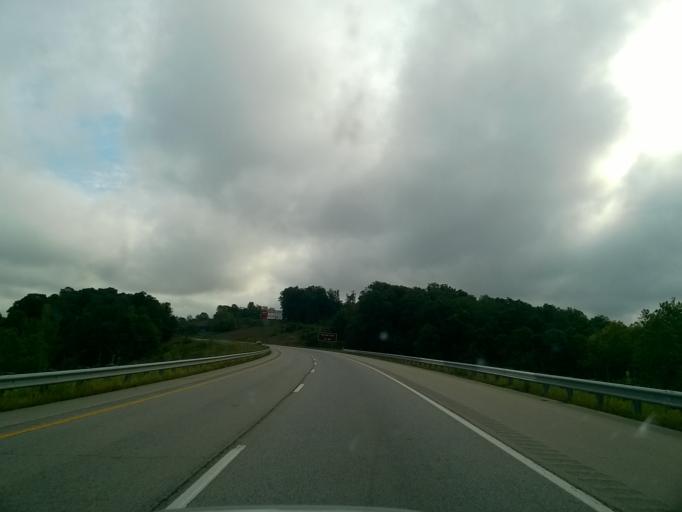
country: US
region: Indiana
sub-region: Crawford County
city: English
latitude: 38.2364
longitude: -86.3708
